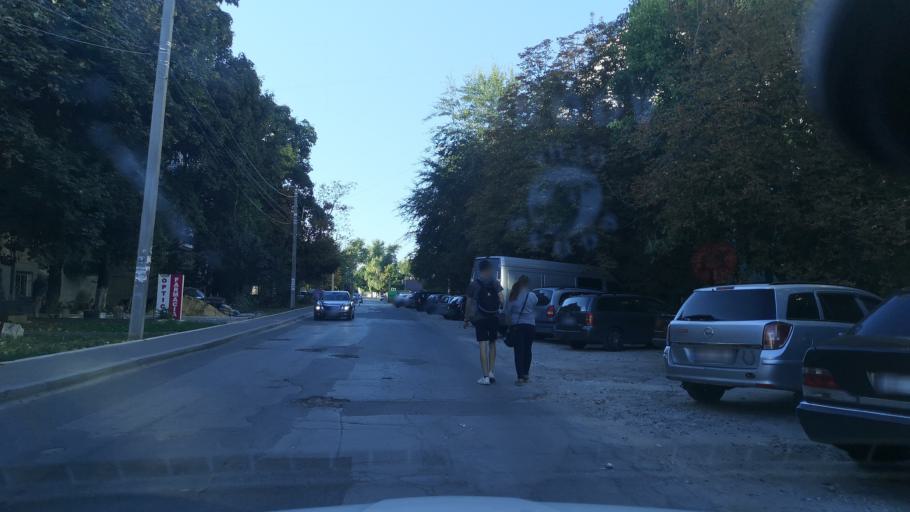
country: MD
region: Chisinau
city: Chisinau
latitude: 46.9883
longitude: 28.8820
